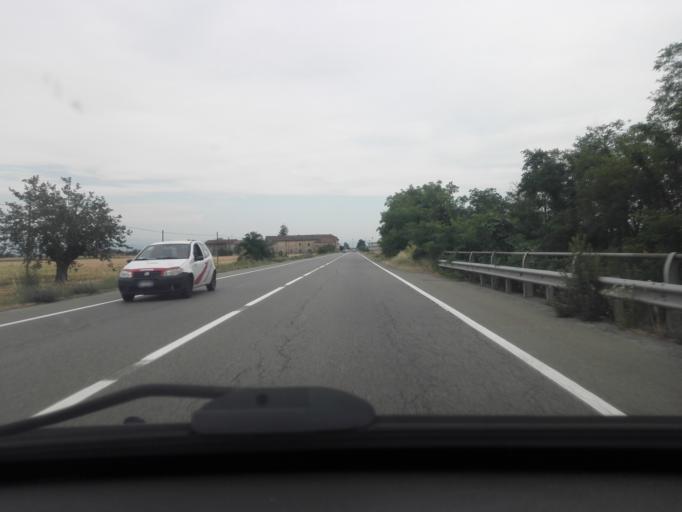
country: IT
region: Piedmont
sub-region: Provincia di Alessandria
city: Mandrogne
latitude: 44.8450
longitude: 8.7256
